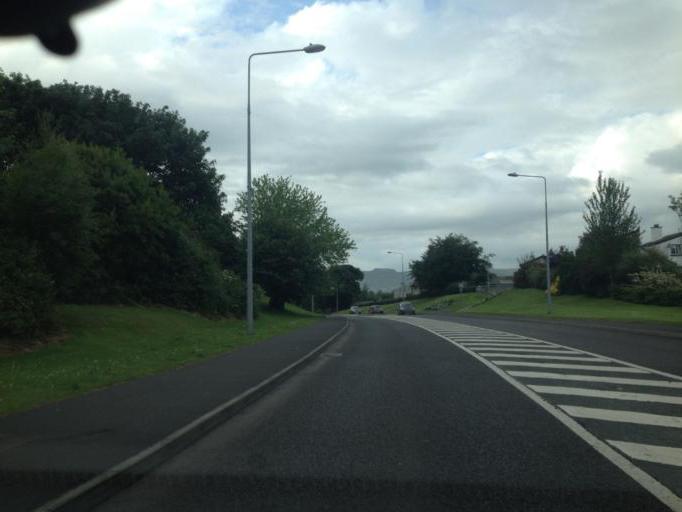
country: IE
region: Connaught
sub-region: Sligo
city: Sligo
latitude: 54.2805
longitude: -8.4724
